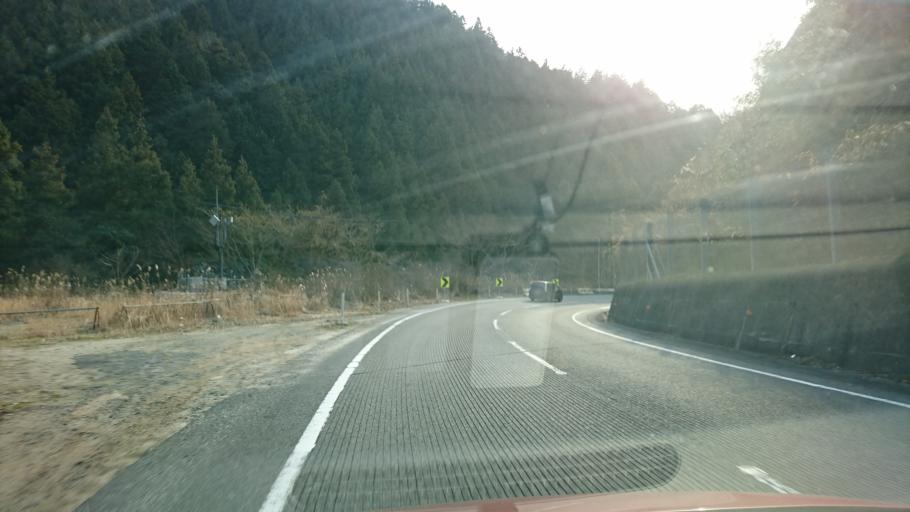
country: JP
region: Ehime
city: Hojo
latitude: 33.9118
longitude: 132.8784
